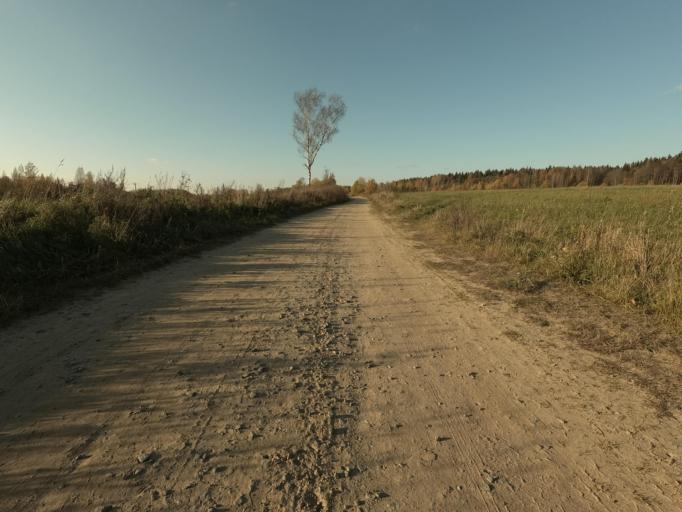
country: RU
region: Leningrad
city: Luppolovo
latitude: 60.1430
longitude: 30.2483
